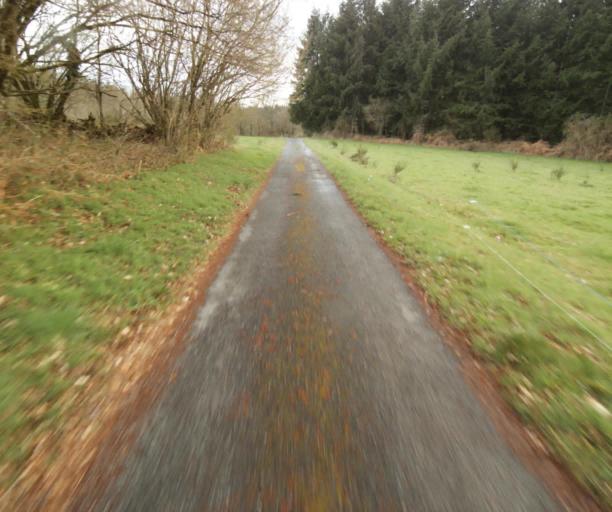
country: FR
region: Limousin
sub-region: Departement de la Correze
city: Saint-Privat
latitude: 45.2258
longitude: 1.9990
